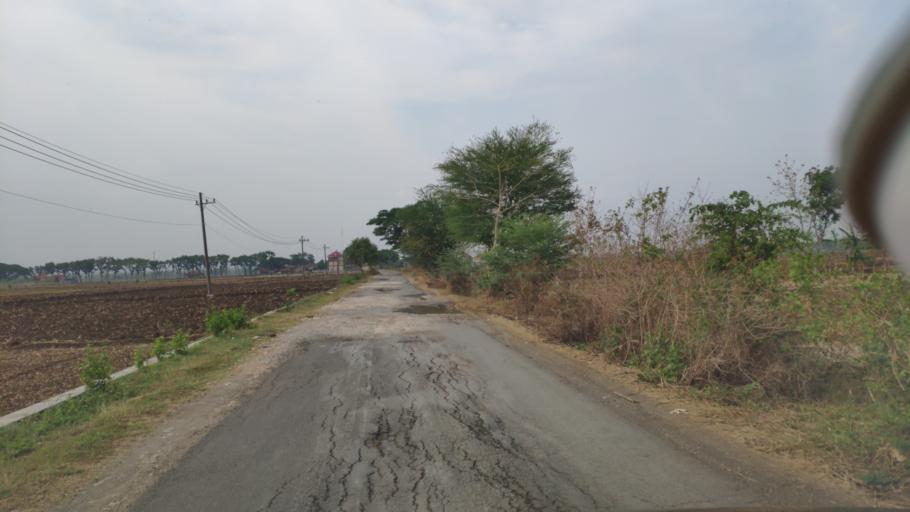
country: ID
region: Central Java
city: Karangtalun
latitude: -7.0139
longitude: 111.3473
